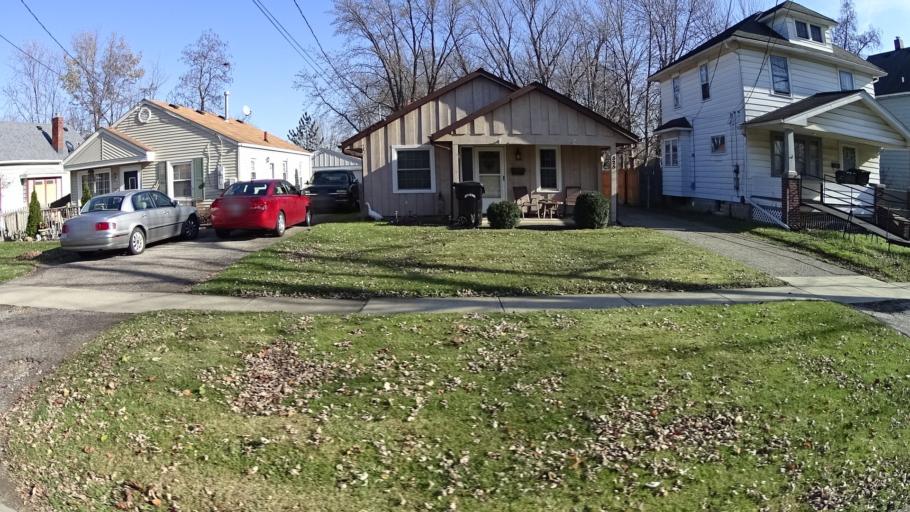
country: US
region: Ohio
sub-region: Lorain County
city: Elyria
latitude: 41.3793
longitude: -82.1115
